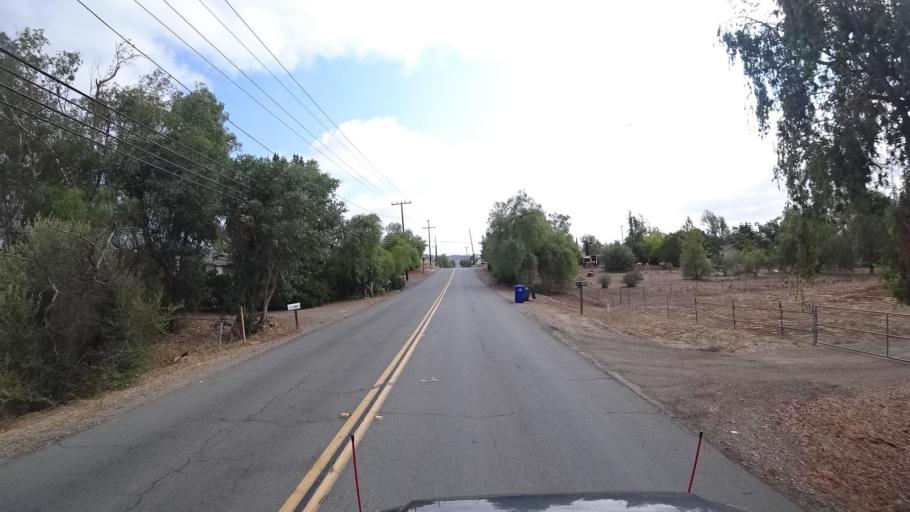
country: US
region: California
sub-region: San Diego County
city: Ramona
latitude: 33.0340
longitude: -116.8493
